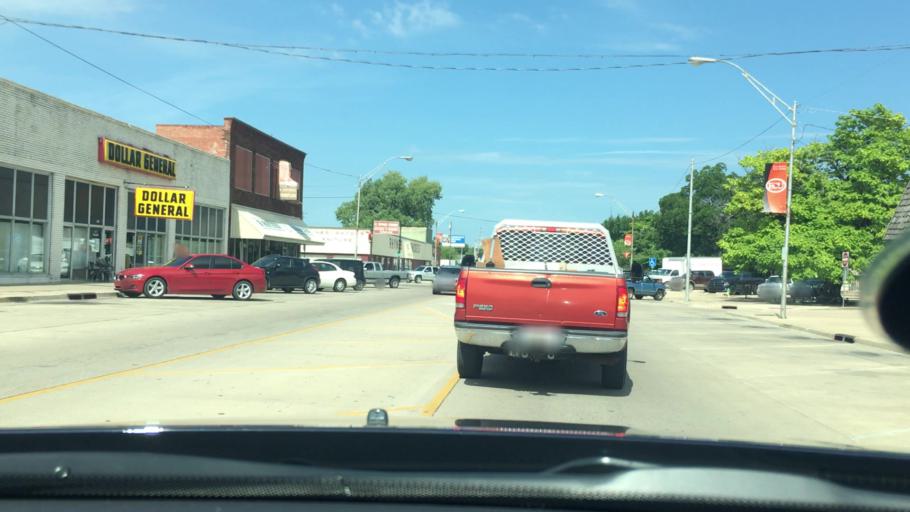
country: US
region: Oklahoma
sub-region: Pontotoc County
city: Ada
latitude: 34.7745
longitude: -96.6810
